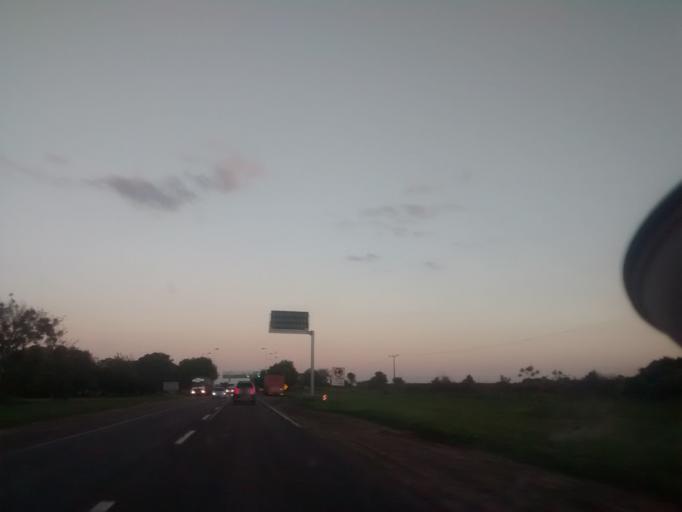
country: AR
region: Chaco
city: Makalle
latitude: -27.1849
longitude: -59.3284
